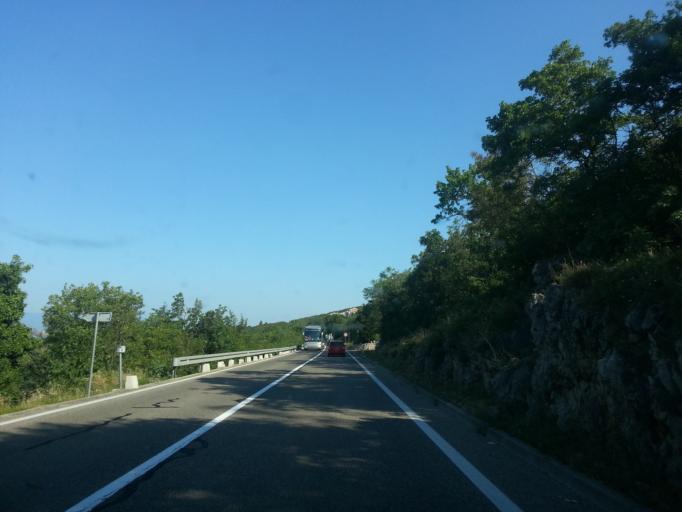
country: HR
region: Primorsko-Goranska
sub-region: Grad Crikvenica
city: Jadranovo
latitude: 45.2081
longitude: 14.6562
